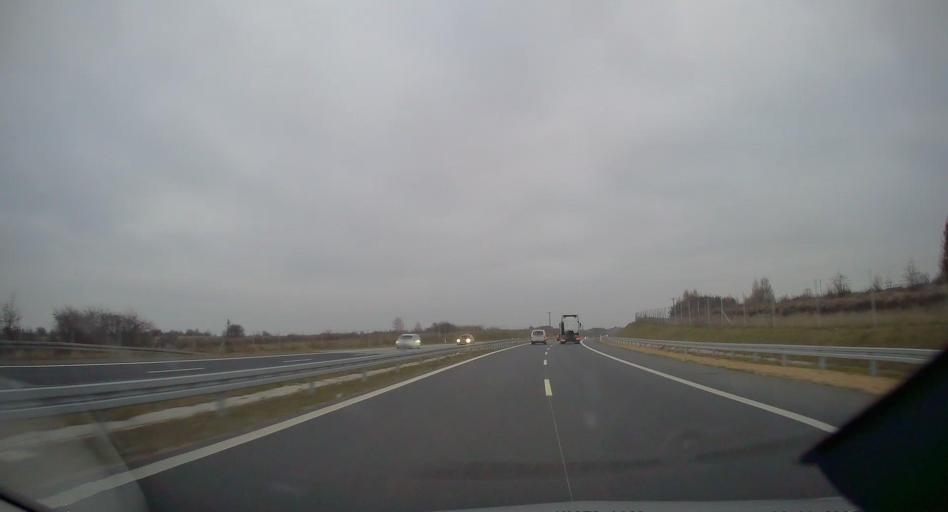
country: PL
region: Silesian Voivodeship
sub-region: Powiat bedzinski
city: Mierzecice
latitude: 50.4428
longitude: 19.1433
